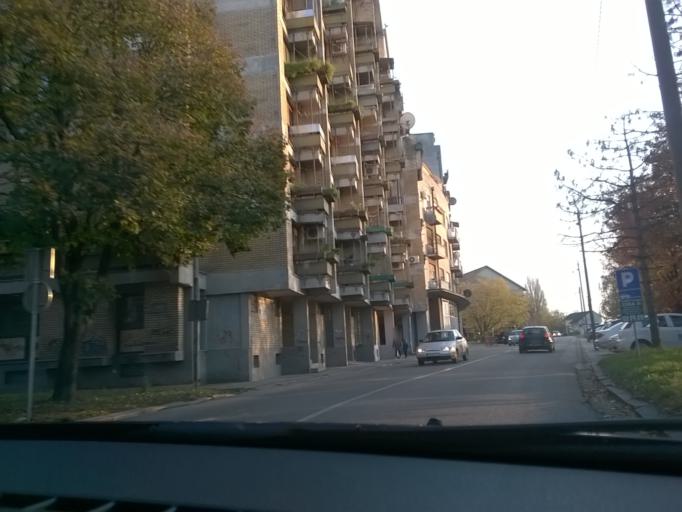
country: RS
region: Autonomna Pokrajina Vojvodina
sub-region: Juznobanatski Okrug
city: Pancevo
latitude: 44.8669
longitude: 20.6397
